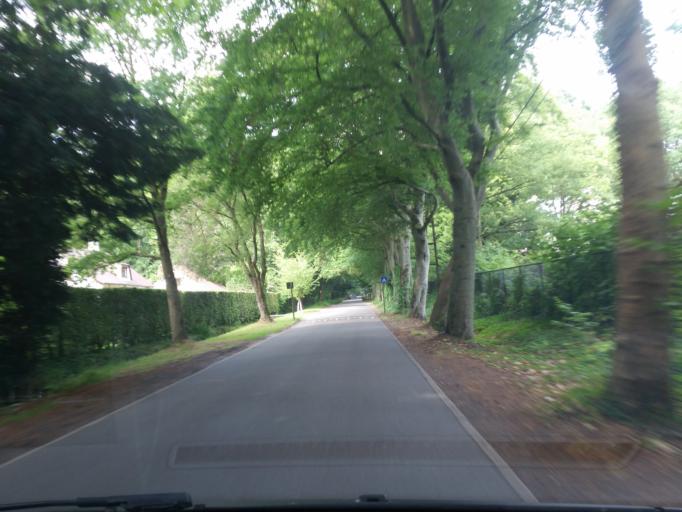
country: BE
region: Flanders
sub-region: Provincie Antwerpen
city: Brasschaat
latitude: 51.3053
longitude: 4.5315
